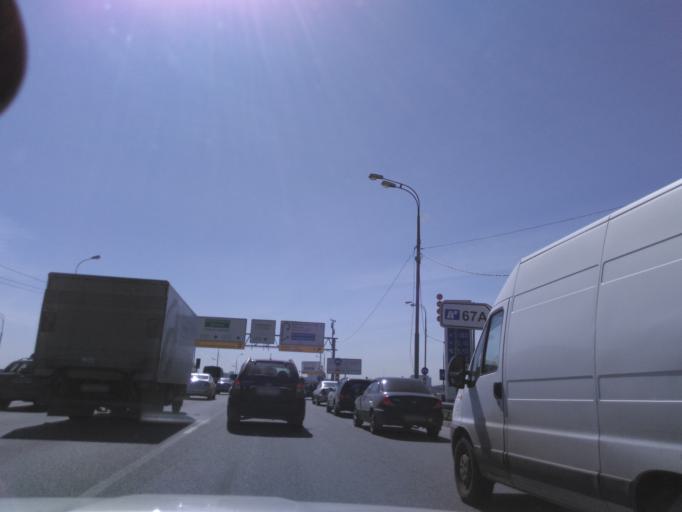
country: RU
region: Moscow
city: Strogino
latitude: 55.8359
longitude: 37.3958
